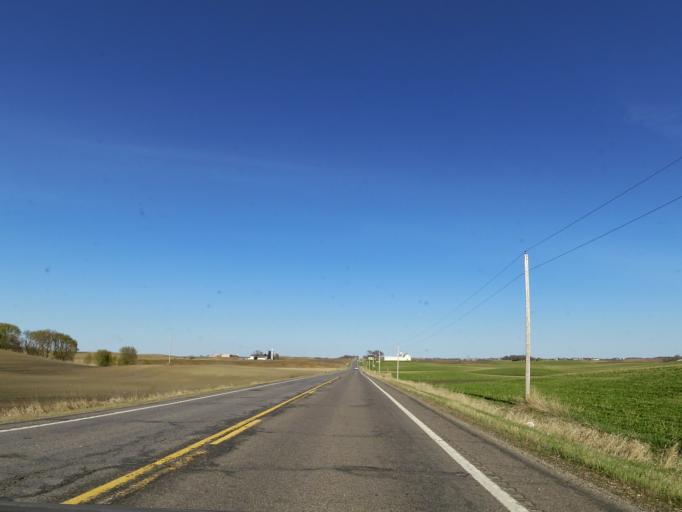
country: US
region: Minnesota
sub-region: Scott County
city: Elko New Market
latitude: 44.5728
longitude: -93.3940
